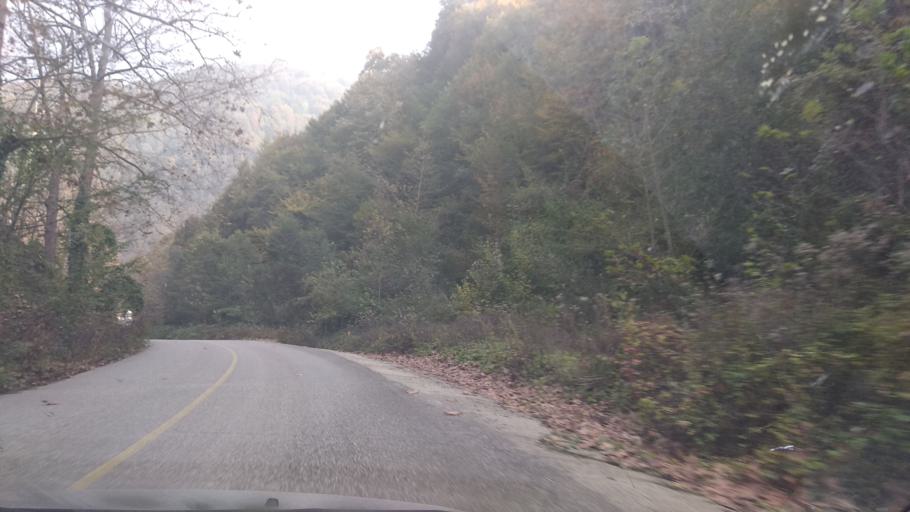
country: TR
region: Duzce
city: Kaynasli
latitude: 40.7268
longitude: 31.2565
